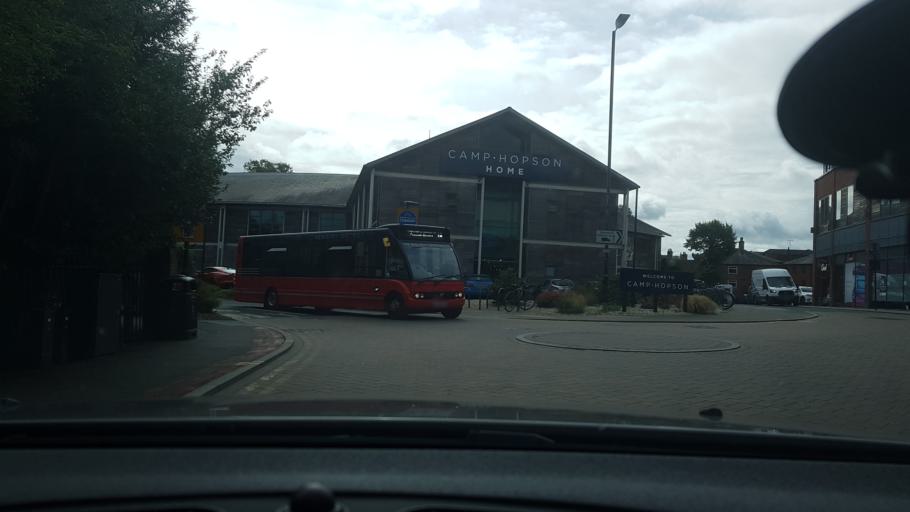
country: GB
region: England
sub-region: West Berkshire
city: Newbury
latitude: 51.4032
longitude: -1.3223
